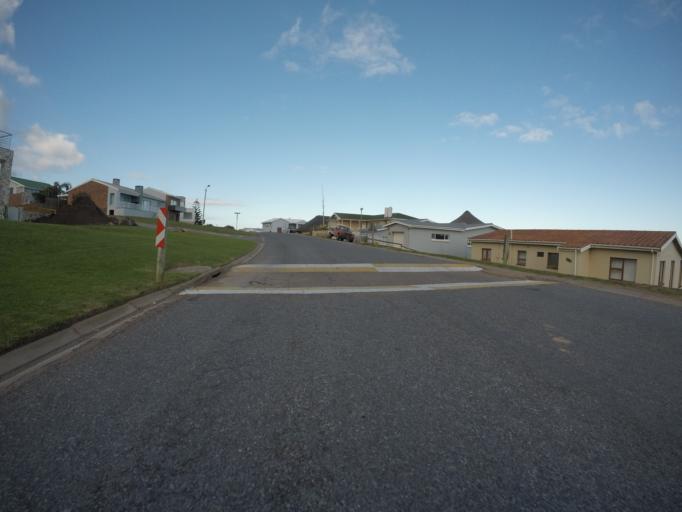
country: ZA
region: Western Cape
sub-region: Eden District Municipality
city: Riversdale
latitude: -34.4253
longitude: 21.3410
